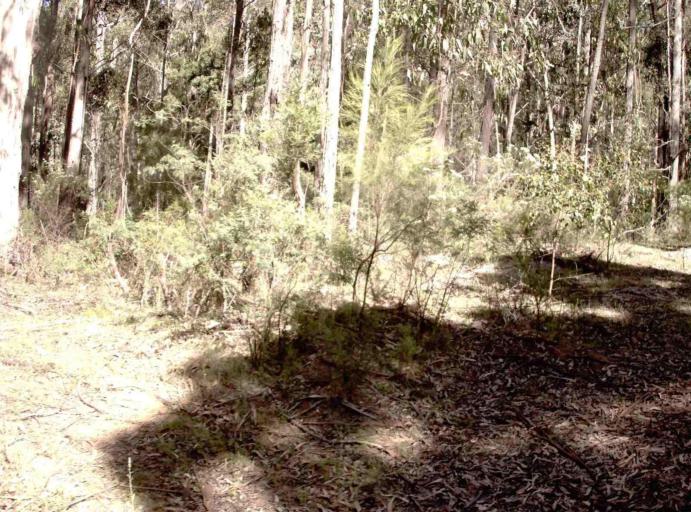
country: AU
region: New South Wales
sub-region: Bombala
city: Bombala
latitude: -37.2878
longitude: 148.7149
